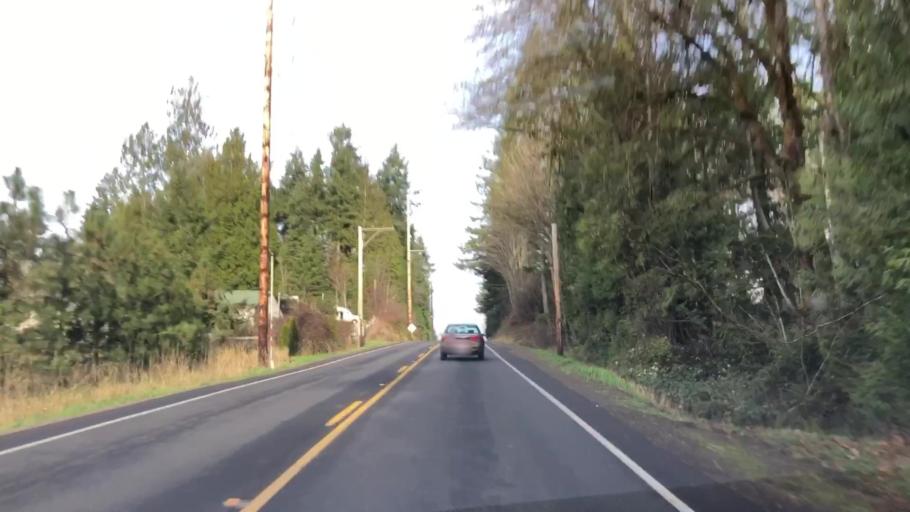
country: US
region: Washington
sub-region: Kitsap County
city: Kingston
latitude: 47.7909
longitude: -122.5414
